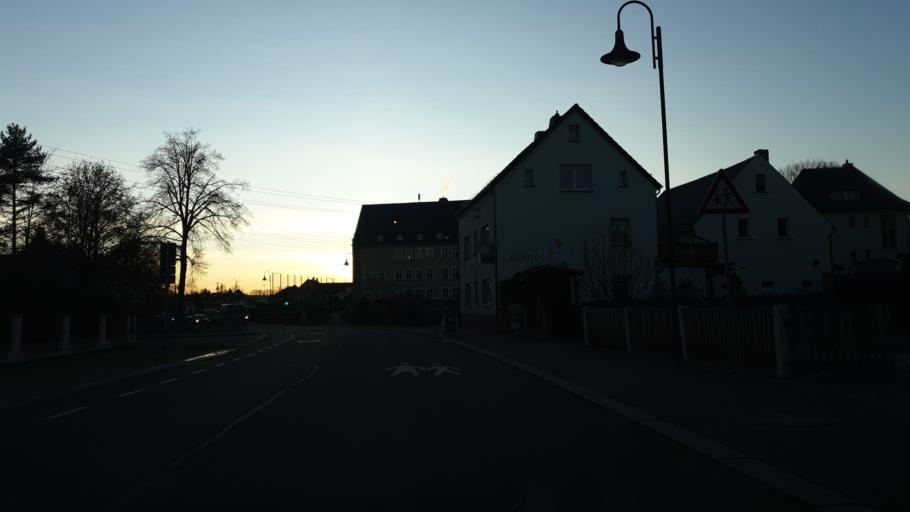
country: DE
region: Saxony
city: Kirchberg
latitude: 50.7915
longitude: 12.7510
